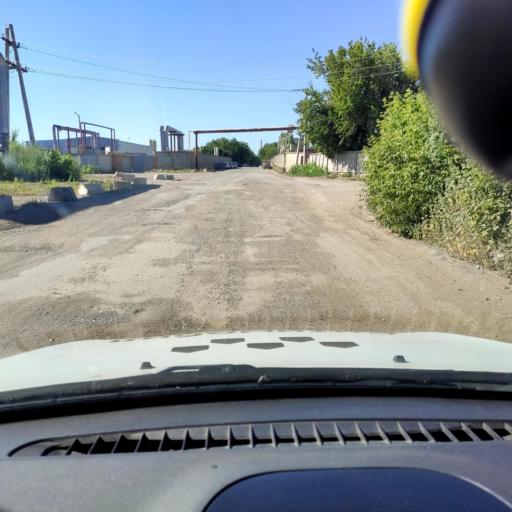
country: RU
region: Samara
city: Tol'yatti
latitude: 53.5872
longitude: 49.2578
